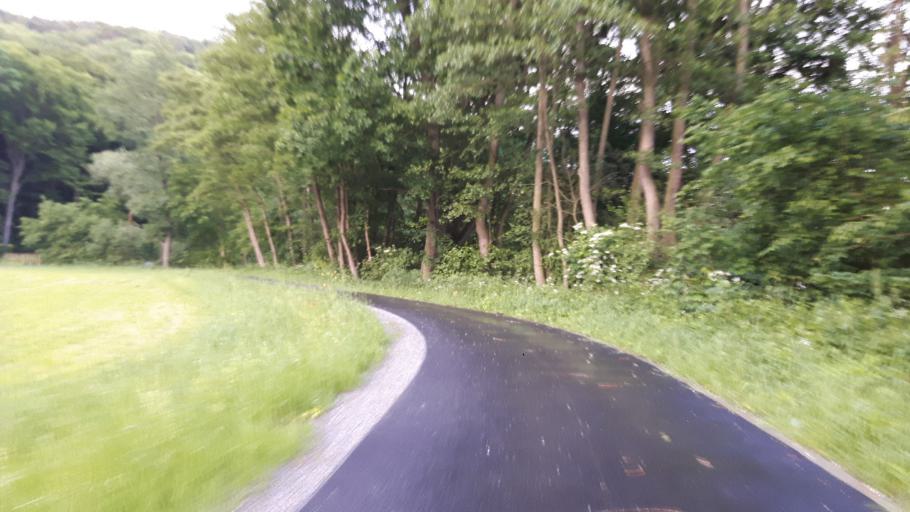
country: DE
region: Thuringia
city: Hetschburg
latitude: 50.9179
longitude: 11.3131
